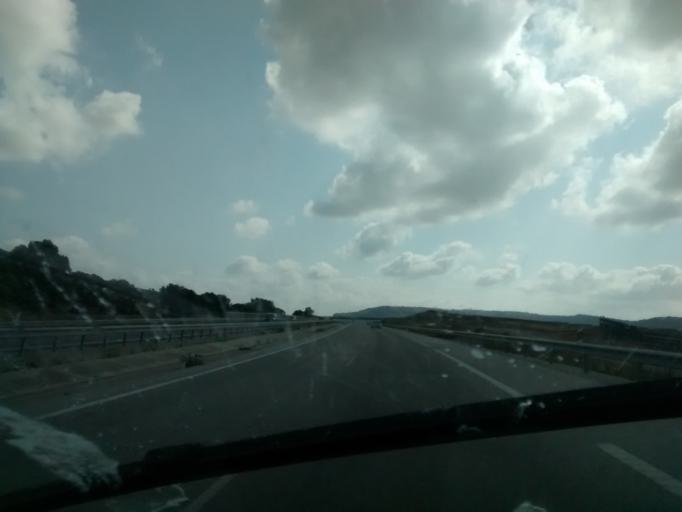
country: ES
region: Andalusia
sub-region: Provincia de Cadiz
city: Vejer de la Frontera
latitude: 36.2493
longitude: -6.0159
